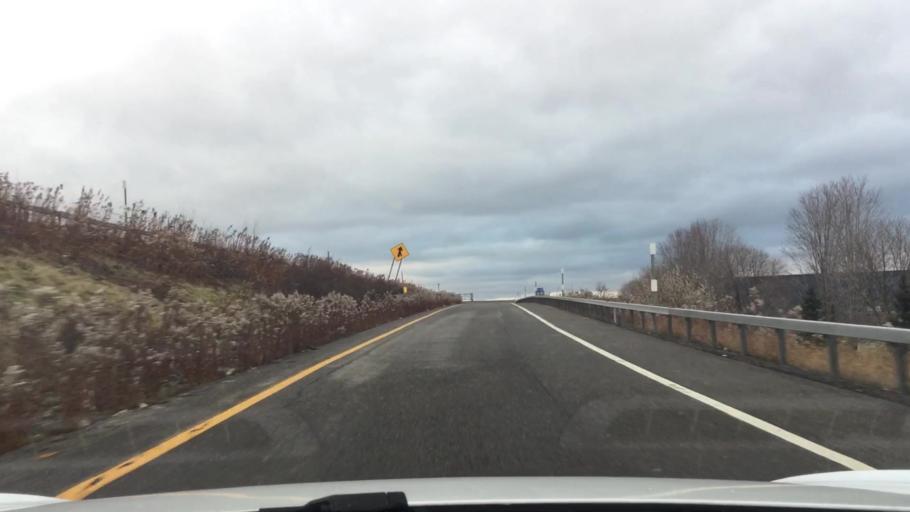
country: US
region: New York
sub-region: Niagara County
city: Niagara Falls
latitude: 43.0817
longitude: -78.9904
